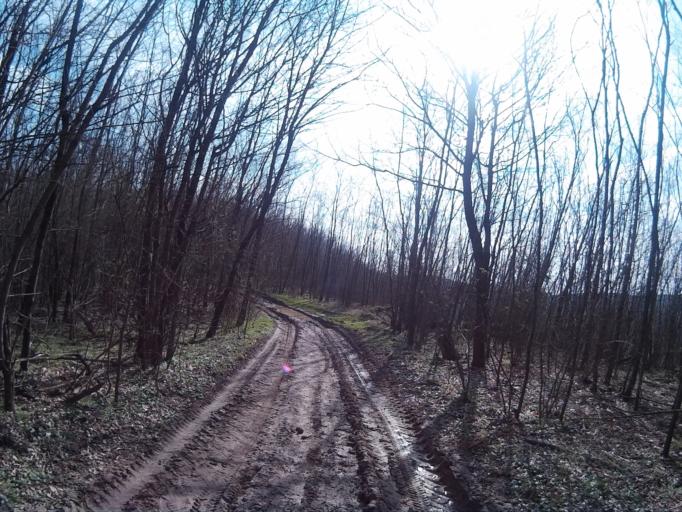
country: HU
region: Pest
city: Kosd
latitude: 47.8643
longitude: 19.2080
